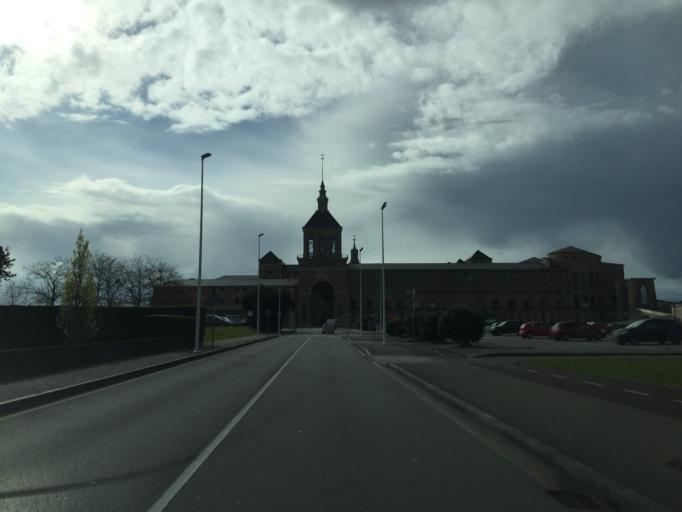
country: ES
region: Asturias
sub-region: Province of Asturias
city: Gijon
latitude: 43.5240
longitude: -5.6116
